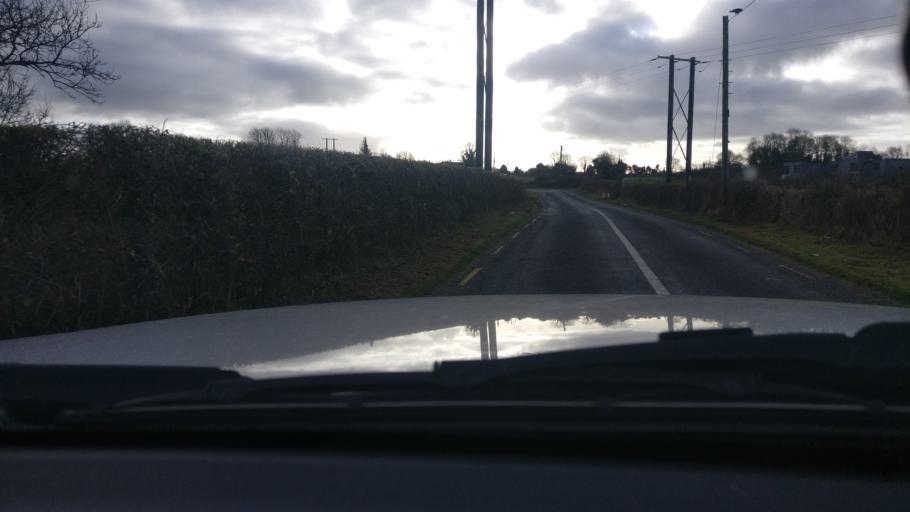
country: IE
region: Connaught
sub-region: County Galway
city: Ballinasloe
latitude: 53.2861
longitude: -8.2412
